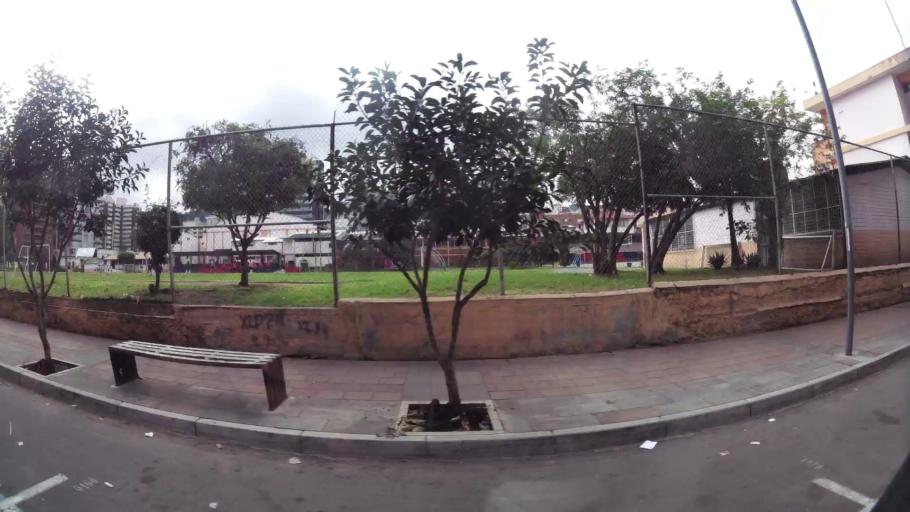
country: EC
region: Pichincha
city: Quito
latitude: -0.1828
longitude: -78.4804
